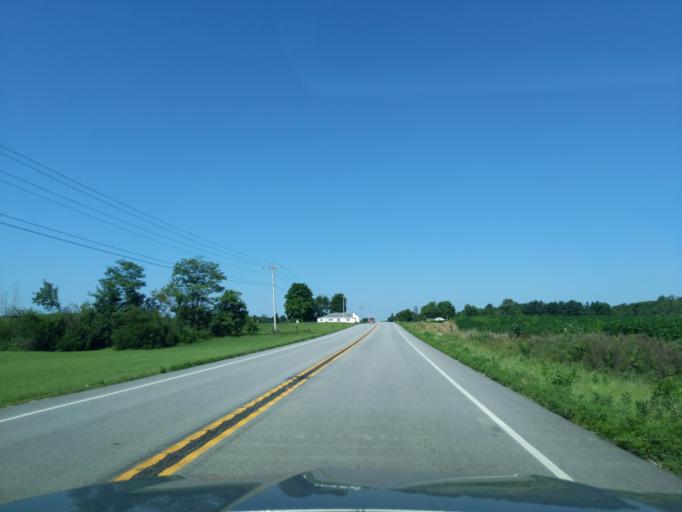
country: US
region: Indiana
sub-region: Ripley County
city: Versailles
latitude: 39.0748
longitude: -85.3079
